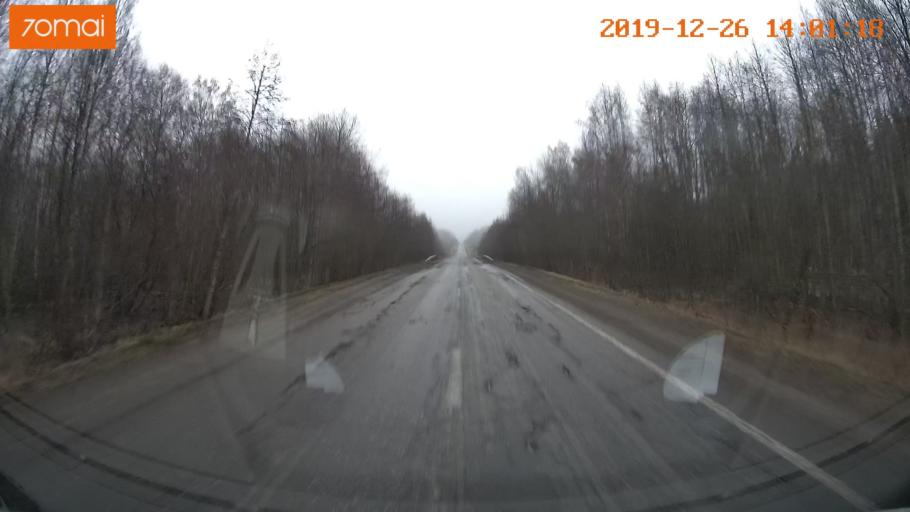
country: RU
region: Jaroslavl
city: Poshekhon'ye
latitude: 58.5514
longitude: 38.7614
